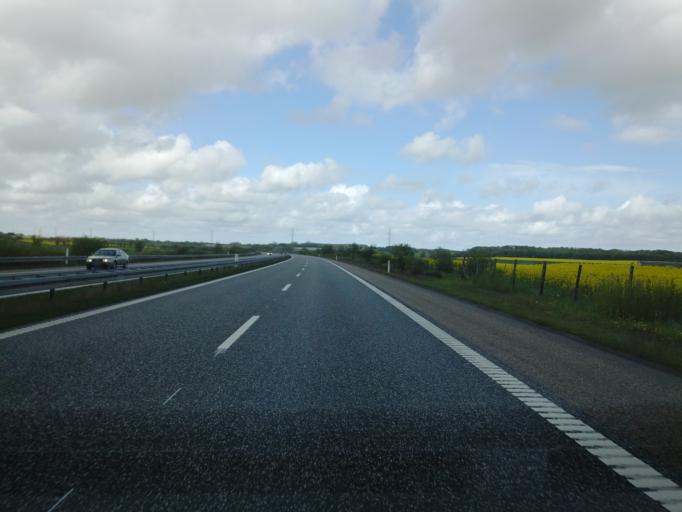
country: DK
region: North Denmark
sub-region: Bronderslev Kommune
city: Dronninglund
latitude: 57.2630
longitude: 10.3665
